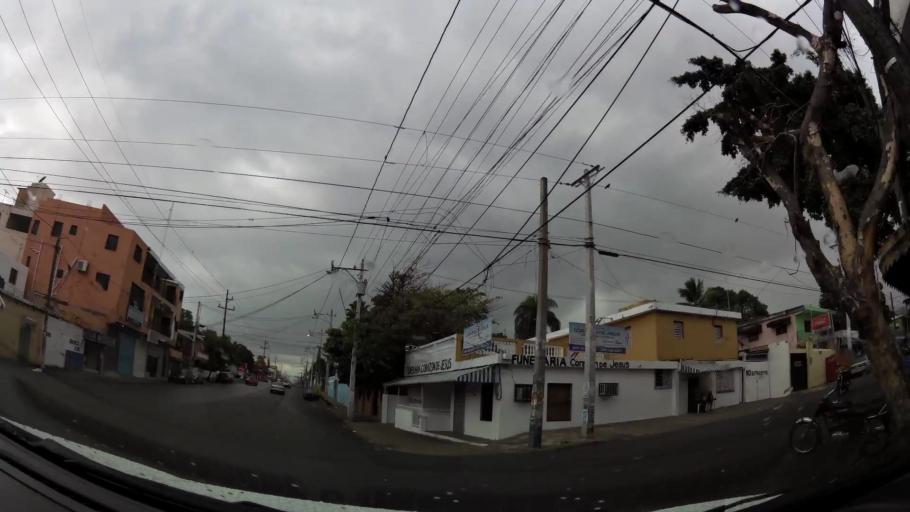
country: DO
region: Nacional
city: La Agustina
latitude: 18.4997
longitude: -69.9196
